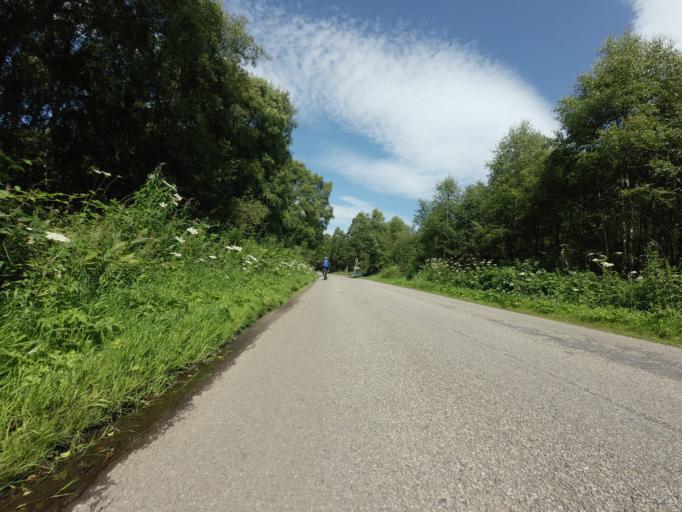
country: GB
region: Scotland
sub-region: Highland
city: Inverness
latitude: 57.5331
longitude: -4.3219
